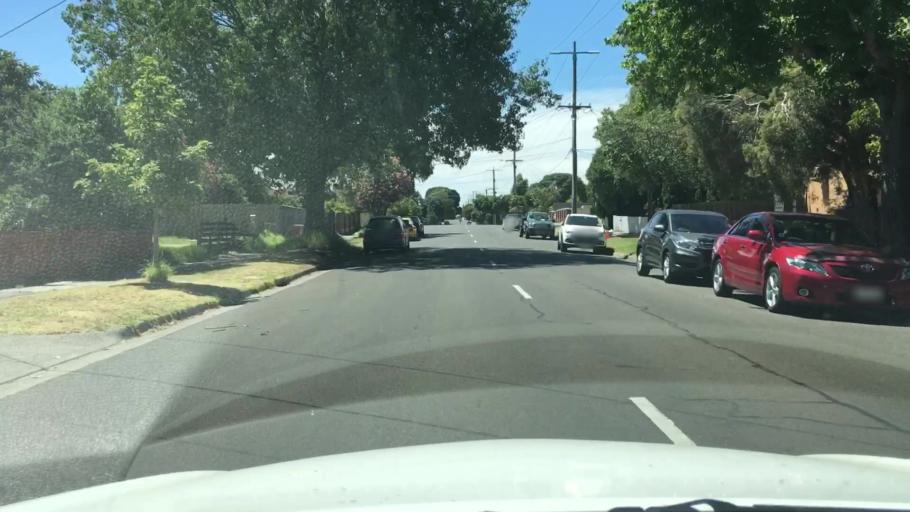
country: AU
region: Victoria
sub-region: Greater Dandenong
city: Springvale
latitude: -37.9548
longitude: 145.1428
